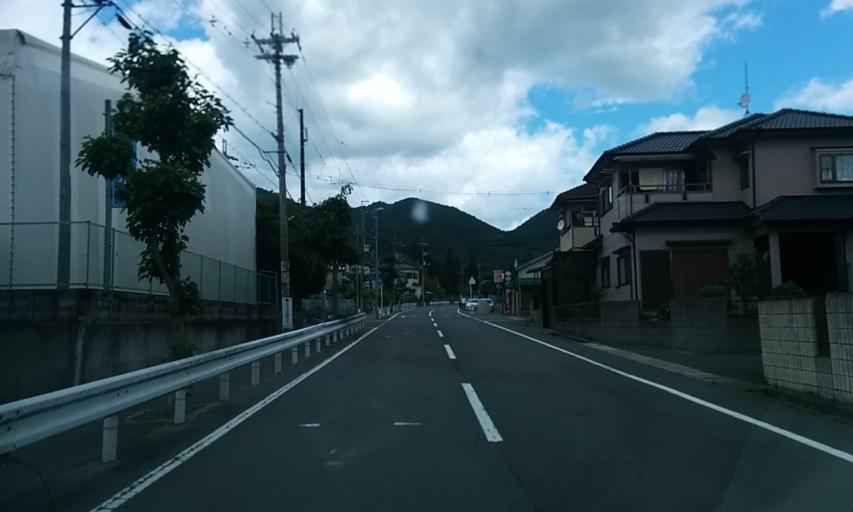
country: JP
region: Kyoto
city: Kameoka
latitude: 35.0094
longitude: 135.4310
